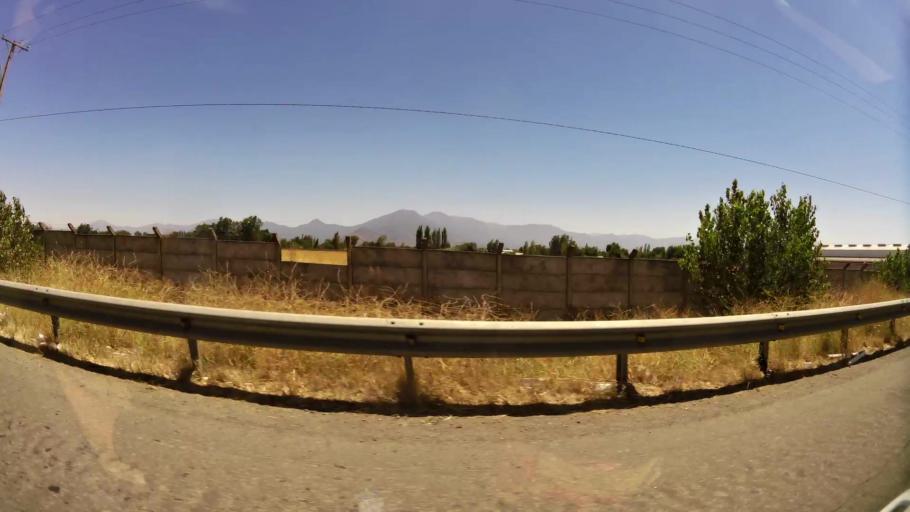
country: CL
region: O'Higgins
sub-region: Provincia de Cachapoal
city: Rancagua
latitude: -34.2215
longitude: -70.7778
